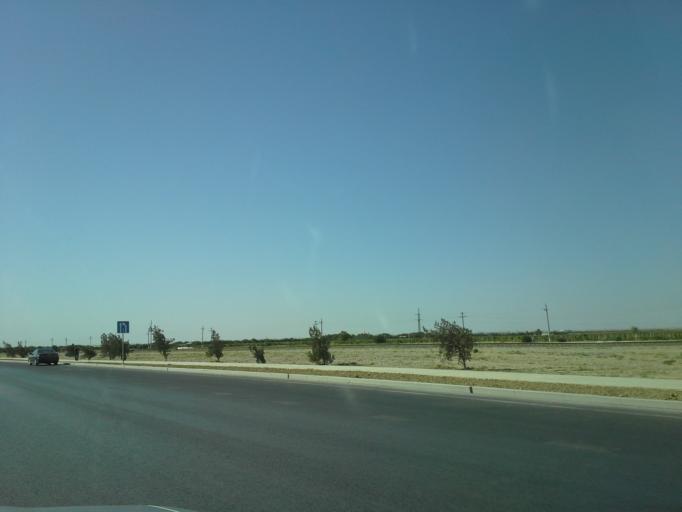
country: TM
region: Ahal
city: Annau
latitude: 37.9145
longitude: 58.4798
